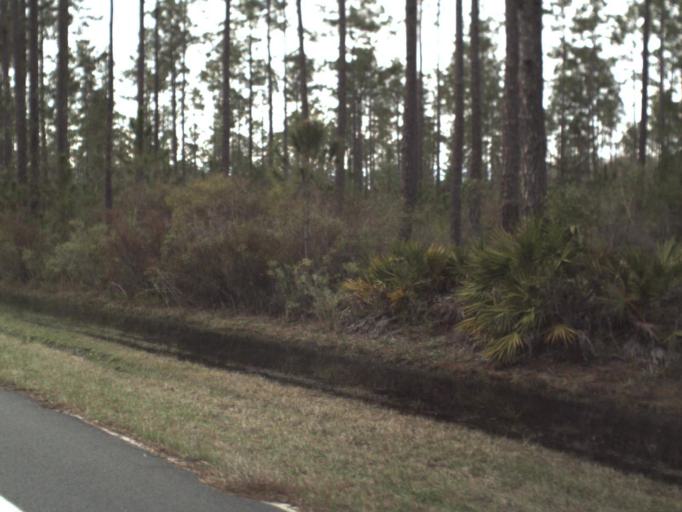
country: US
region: Florida
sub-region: Gulf County
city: Wewahitchka
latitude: 30.1437
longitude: -85.2947
